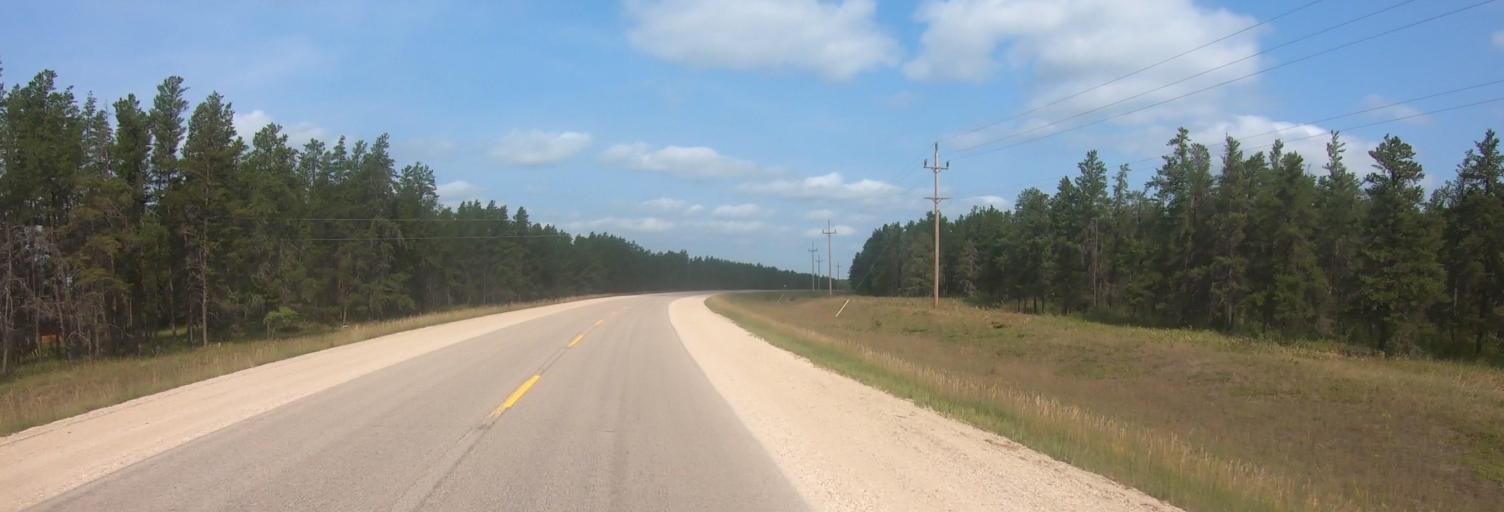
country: CA
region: Manitoba
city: La Broquerie
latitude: 49.2380
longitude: -96.3463
